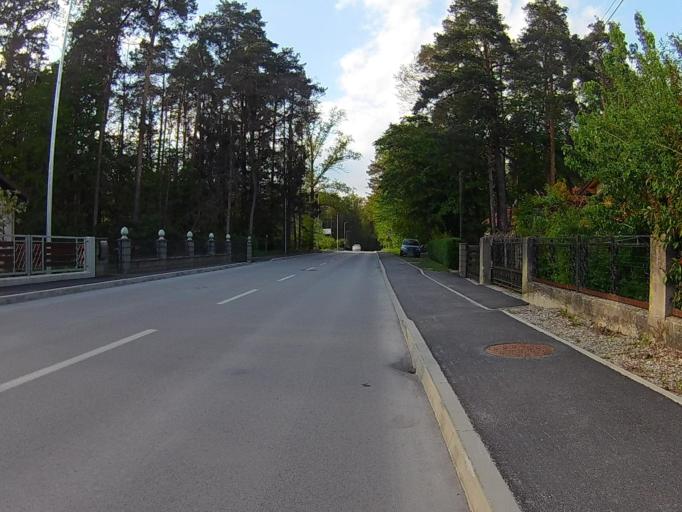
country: SI
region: Miklavz na Dravskem Polju
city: Miklavz na Dravskem Polju
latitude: 46.4853
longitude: 15.7005
